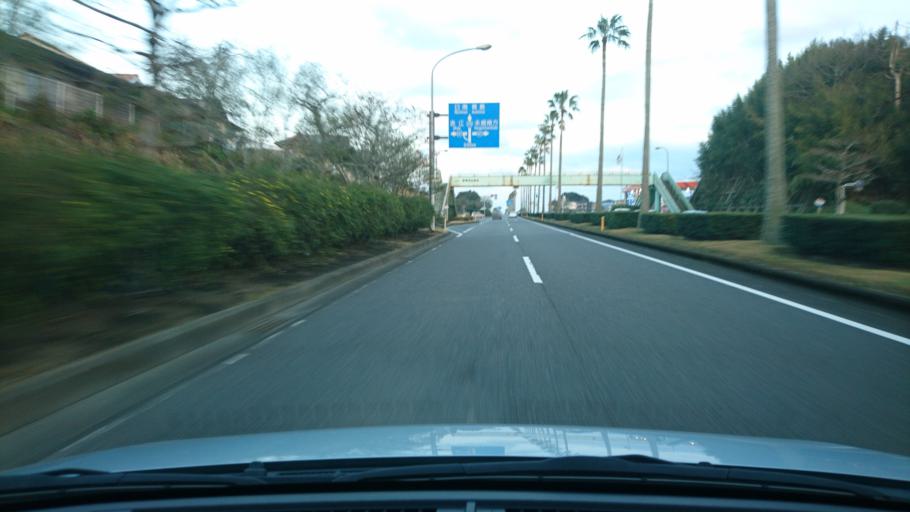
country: JP
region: Miyazaki
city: Miyazaki-shi
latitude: 31.8681
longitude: 131.4252
